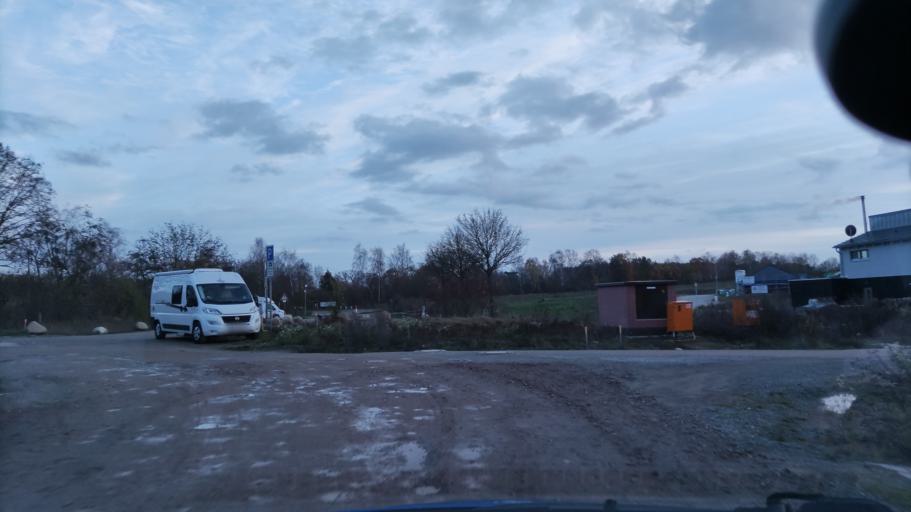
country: DE
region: Lower Saxony
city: Bad Bevensen
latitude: 53.0744
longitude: 10.6007
